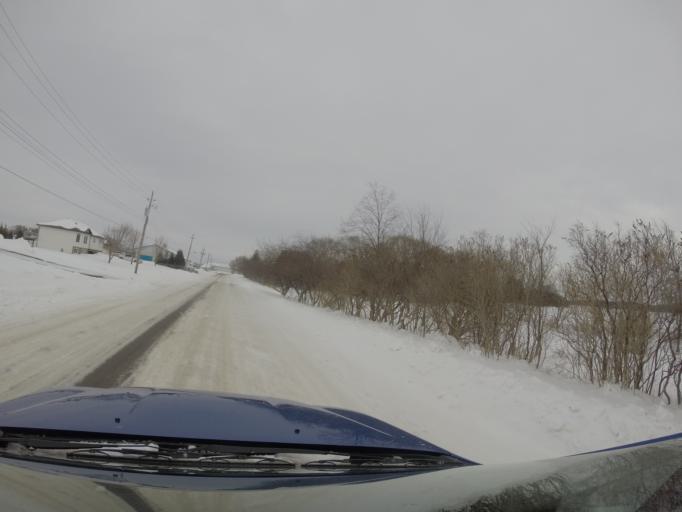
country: CA
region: Ontario
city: Wasaga Beach
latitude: 44.4220
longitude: -80.0655
